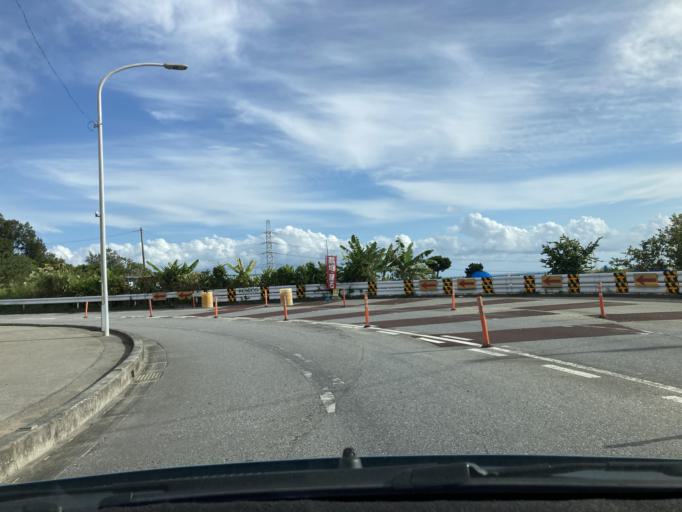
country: JP
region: Okinawa
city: Okinawa
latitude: 26.3383
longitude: 127.8261
